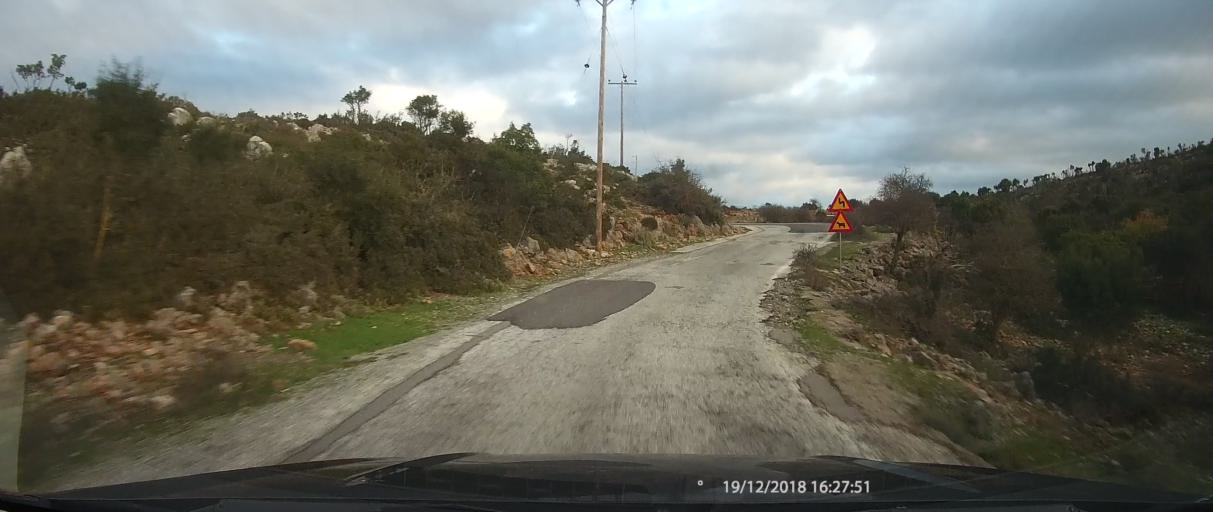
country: GR
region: Peloponnese
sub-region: Nomos Lakonias
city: Kato Glikovrisi
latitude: 36.9614
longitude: 22.8604
